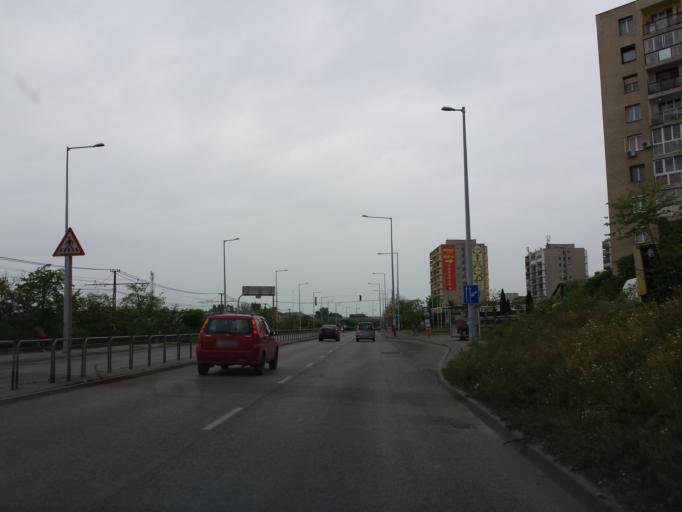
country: HU
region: Budapest
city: Budapest XX. keruelet
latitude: 47.4336
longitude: 19.0981
